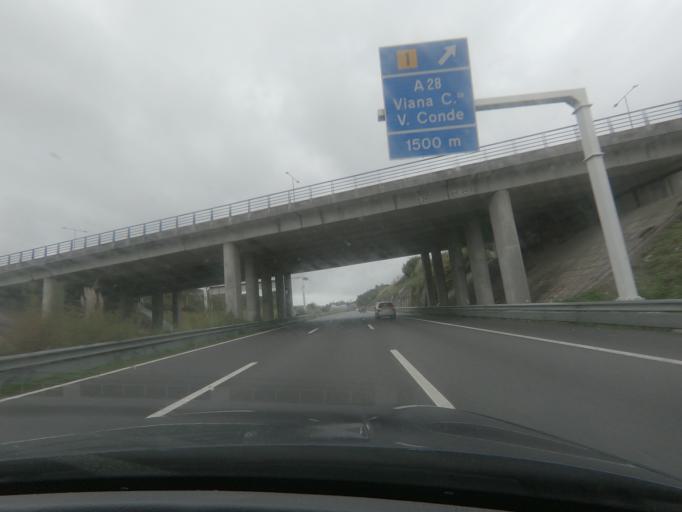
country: PT
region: Porto
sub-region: Matosinhos
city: Santa Cruz do Bispo
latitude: 41.2291
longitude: -8.6766
